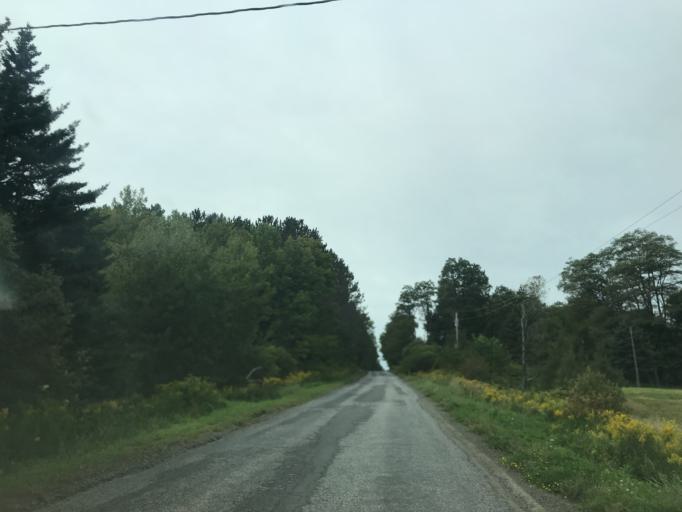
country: US
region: New York
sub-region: Otsego County
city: Worcester
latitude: 42.5952
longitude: -74.6826
